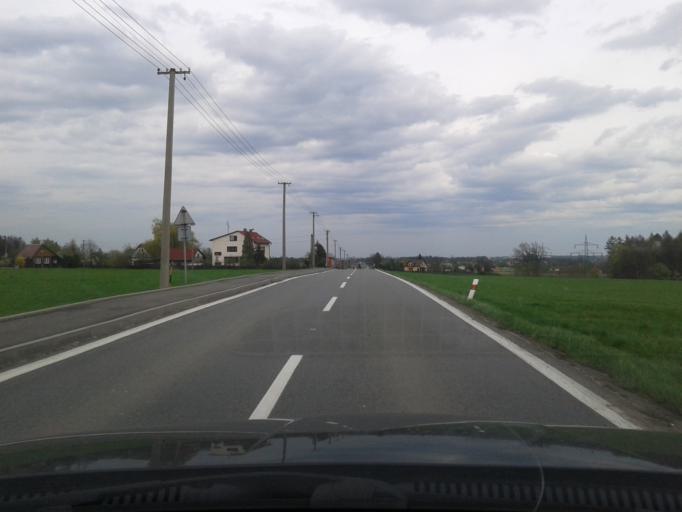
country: CZ
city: Sedliste
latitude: 49.7313
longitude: 18.3656
